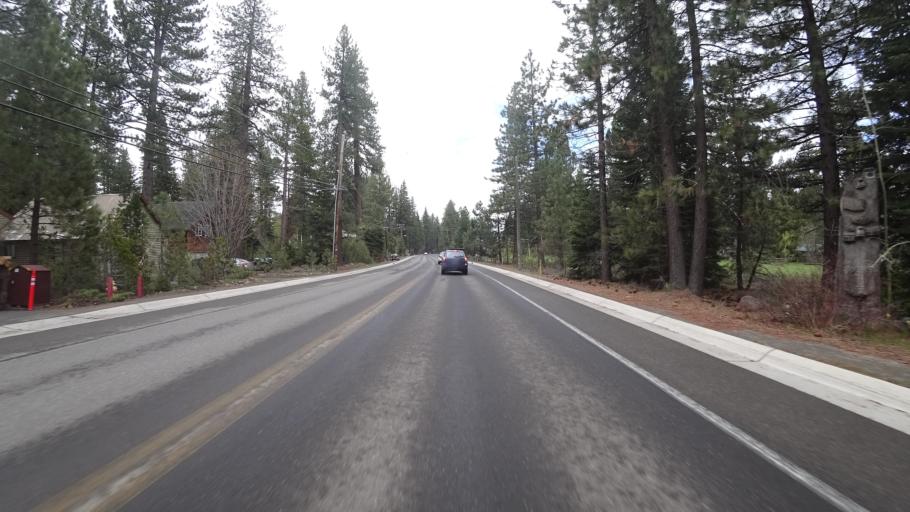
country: US
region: California
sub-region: Placer County
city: Kings Beach
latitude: 39.2447
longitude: -120.0304
